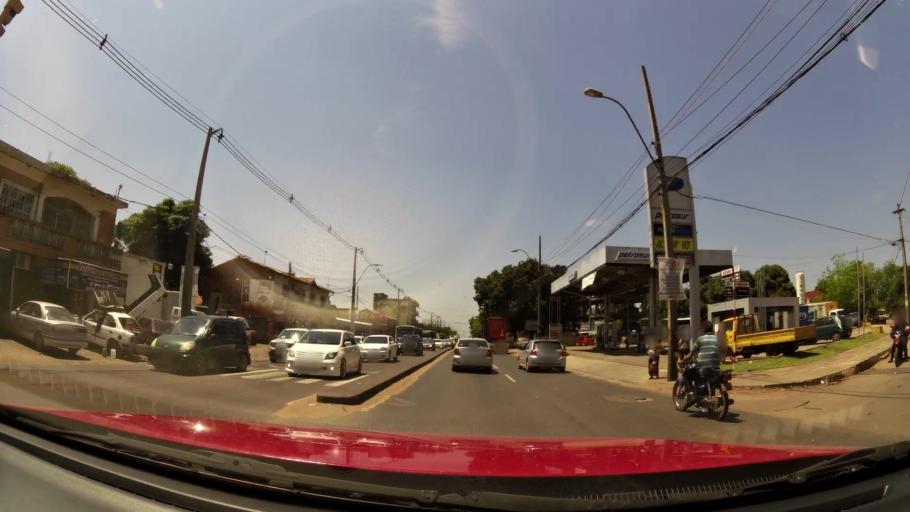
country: PY
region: Central
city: Fernando de la Mora
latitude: -25.3241
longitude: -57.5653
